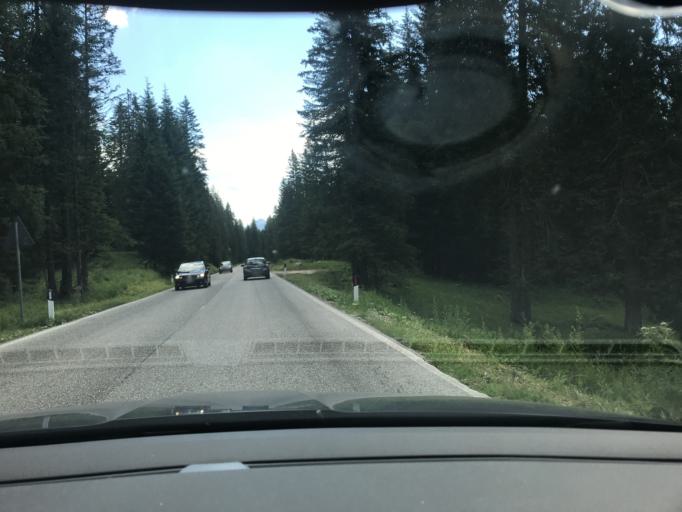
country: IT
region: Veneto
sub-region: Provincia di Belluno
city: Cortina d'Ampezzo
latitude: 46.5206
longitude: 12.0763
